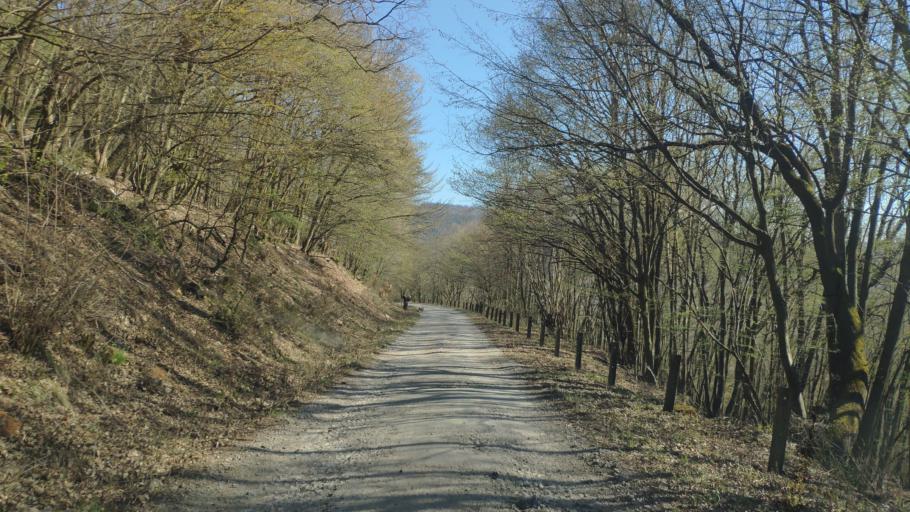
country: SK
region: Kosicky
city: Roznava
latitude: 48.5594
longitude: 20.4059
